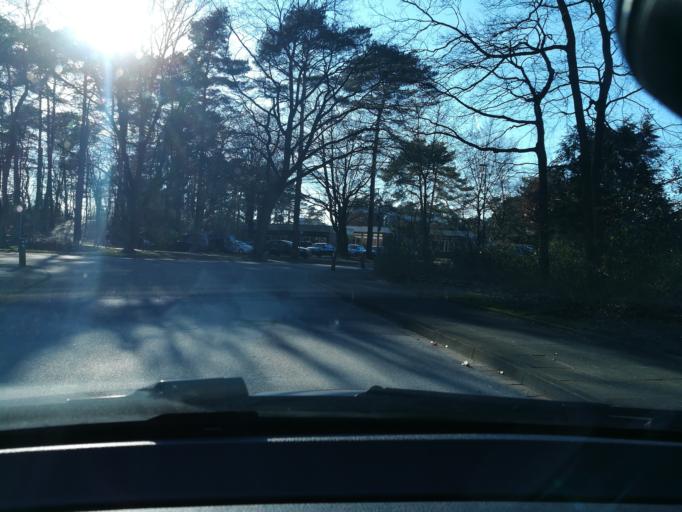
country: DE
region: North Rhine-Westphalia
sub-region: Regierungsbezirk Detmold
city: Oerlinghausen
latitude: 51.9531
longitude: 8.6035
